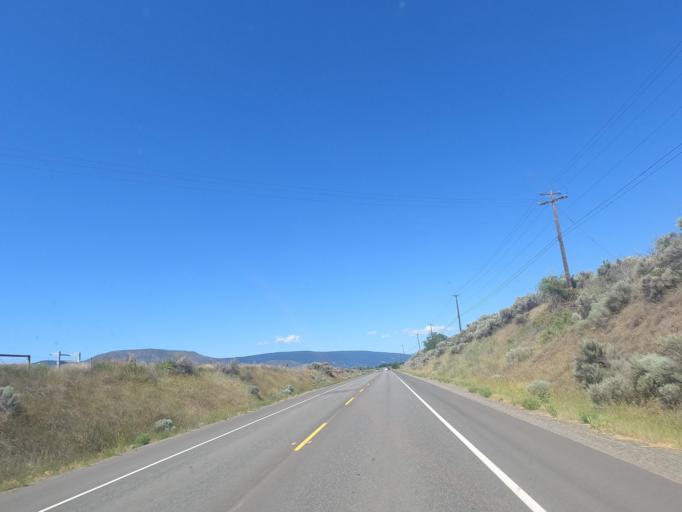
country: CA
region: British Columbia
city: Cache Creek
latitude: 50.7996
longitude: -121.2623
